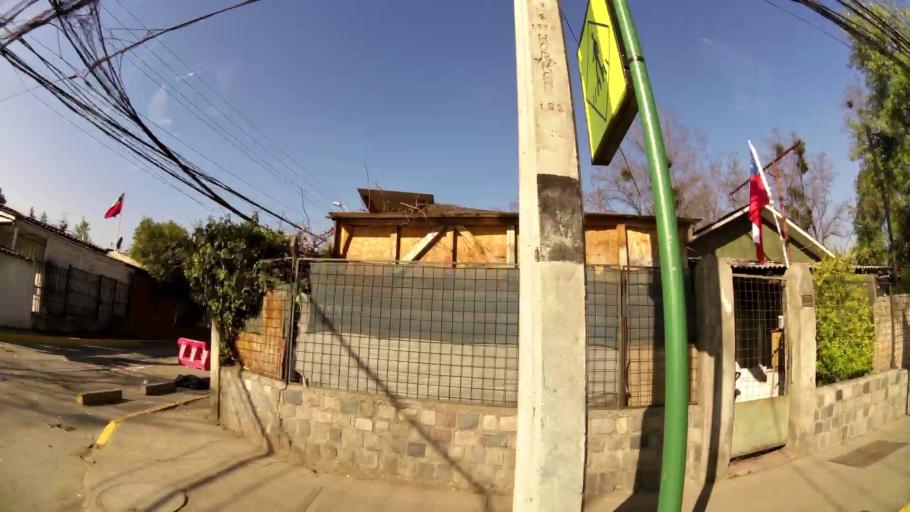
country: CL
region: Santiago Metropolitan
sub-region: Provincia de Santiago
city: Villa Presidente Frei, Nunoa, Santiago, Chile
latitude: -33.3578
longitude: -70.5067
